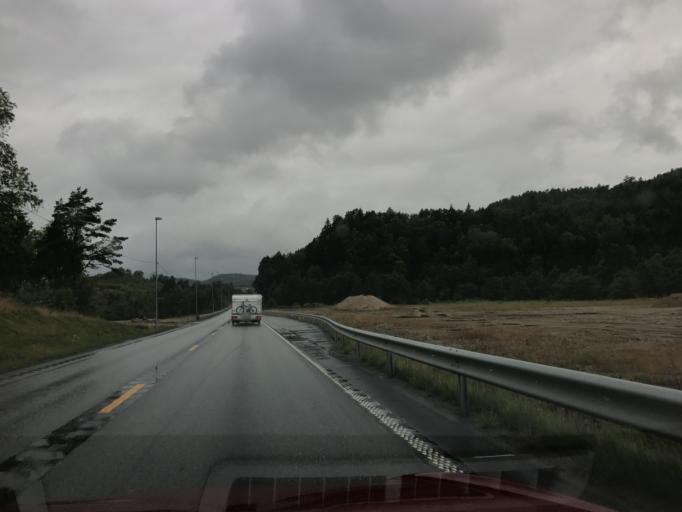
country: NO
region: Vest-Agder
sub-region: Lyngdal
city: Lyngdal
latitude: 58.1541
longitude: 7.1337
